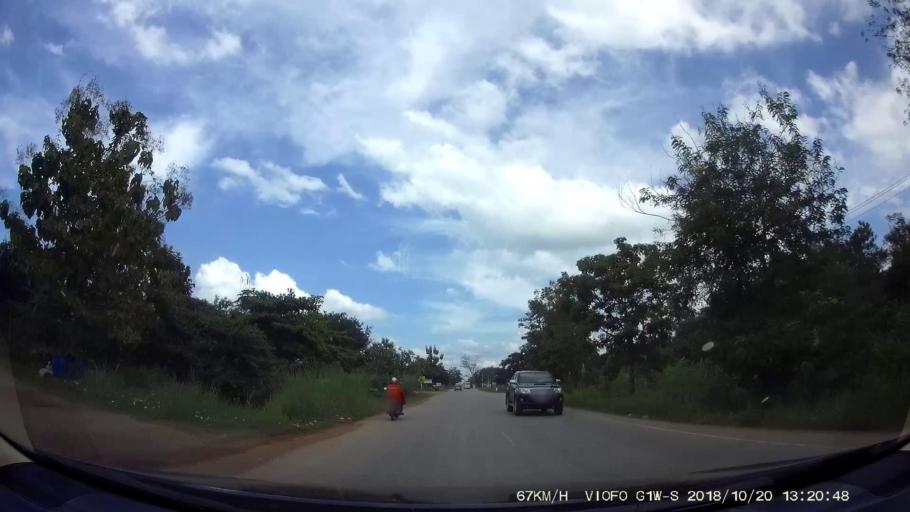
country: TH
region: Chaiyaphum
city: Khon San
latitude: 16.5521
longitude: 101.9061
